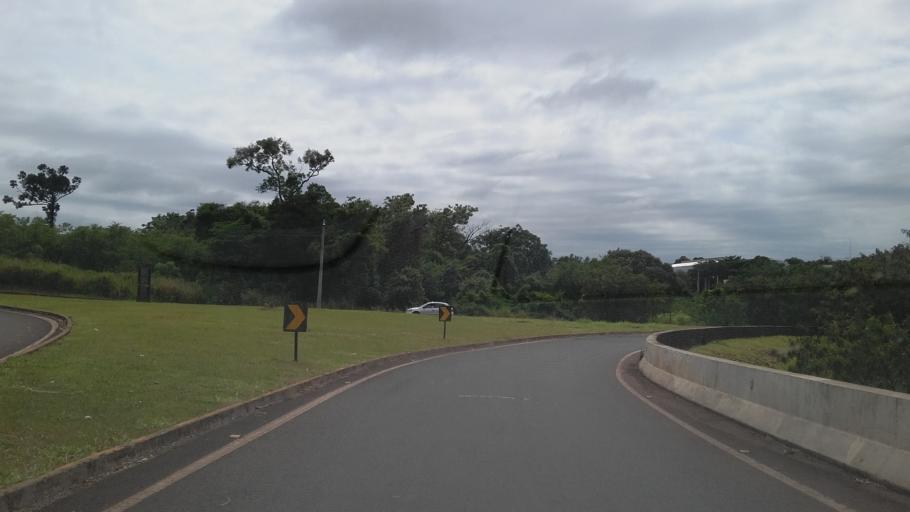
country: BR
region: Parana
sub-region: Londrina
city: Londrina
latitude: -23.2902
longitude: -51.1485
